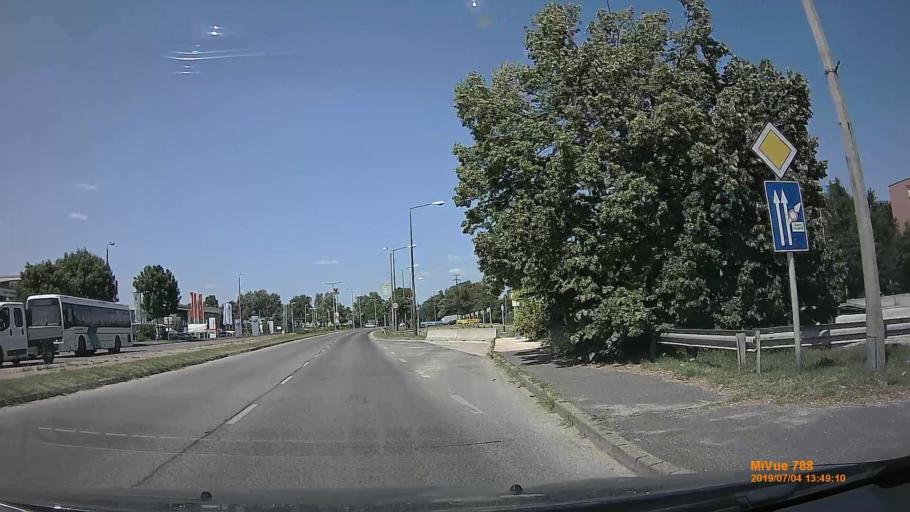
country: HU
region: Komarom-Esztergom
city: Tatabanya
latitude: 47.5946
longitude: 18.3887
